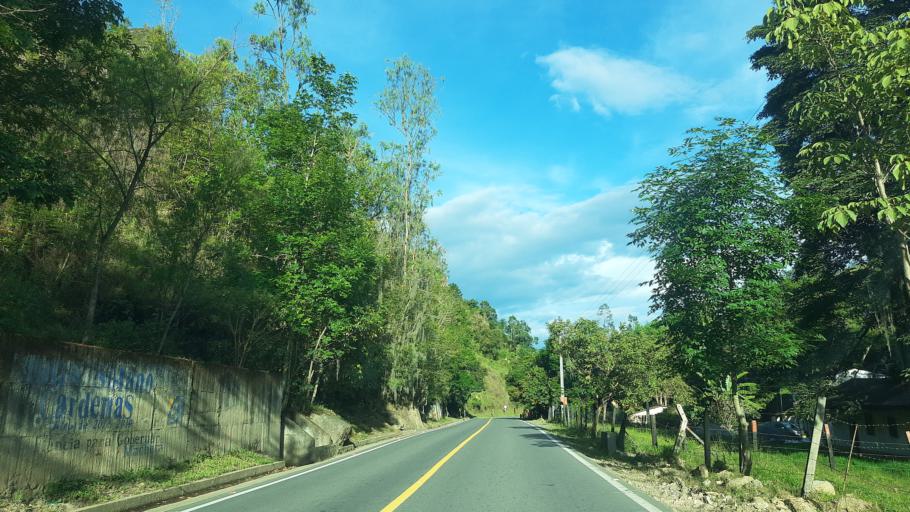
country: CO
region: Cundinamarca
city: Macheta
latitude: 5.0759
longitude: -73.5747
